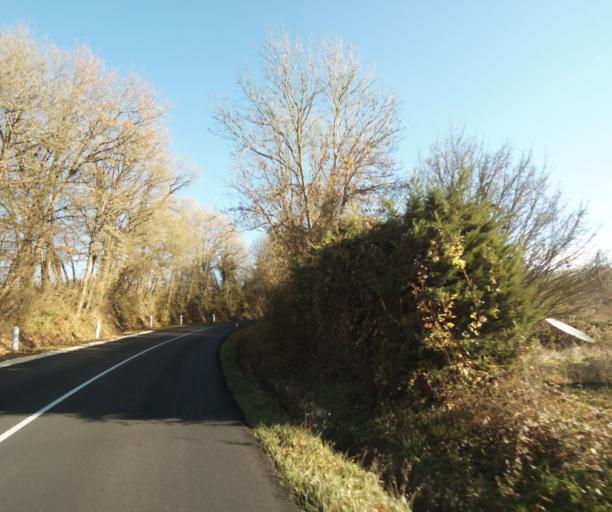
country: FR
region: Poitou-Charentes
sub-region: Departement de la Charente-Maritime
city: Fontcouverte
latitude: 45.7595
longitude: -0.5570
